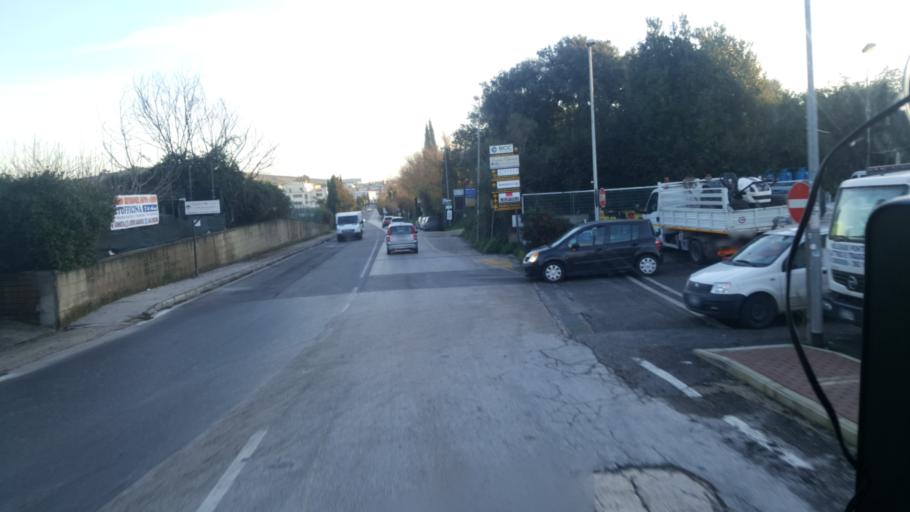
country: IT
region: Latium
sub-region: Citta metropolitana di Roma Capitale
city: Formello
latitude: 42.0471
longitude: 12.3958
